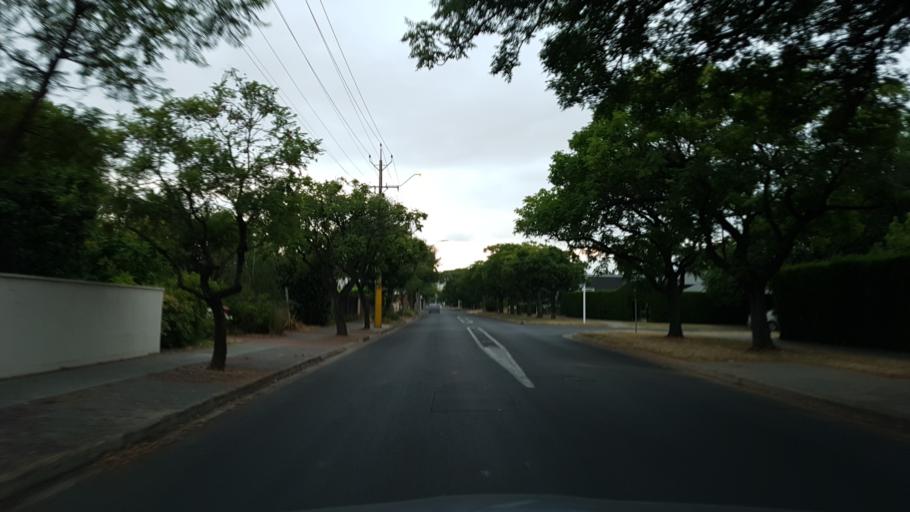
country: AU
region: South Australia
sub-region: Mitcham
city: Hawthorn
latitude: -34.9770
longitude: 138.5958
